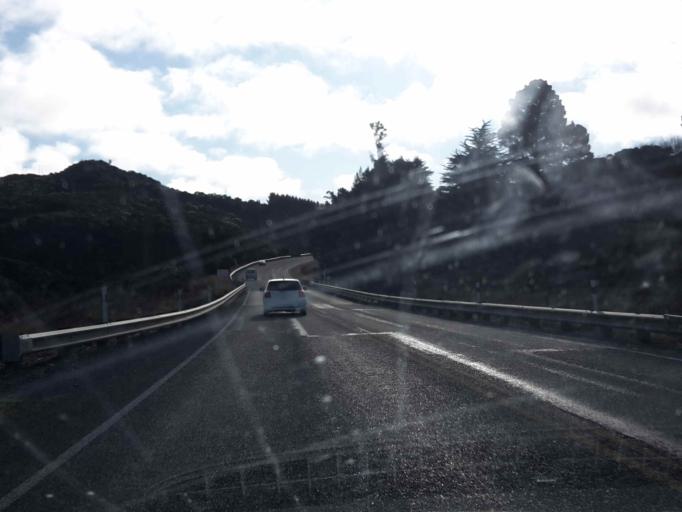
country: NZ
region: Otago
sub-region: Dunedin City
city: Portobello
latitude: -45.7167
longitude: 170.5691
